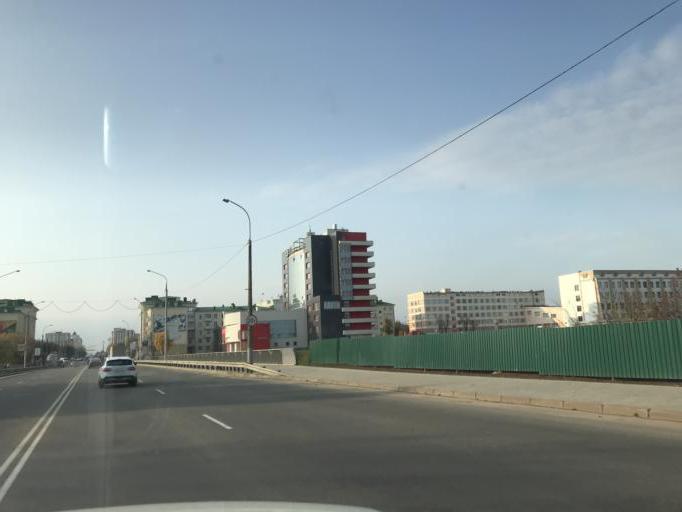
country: BY
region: Mogilev
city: Mahilyow
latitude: 53.9081
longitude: 30.3497
